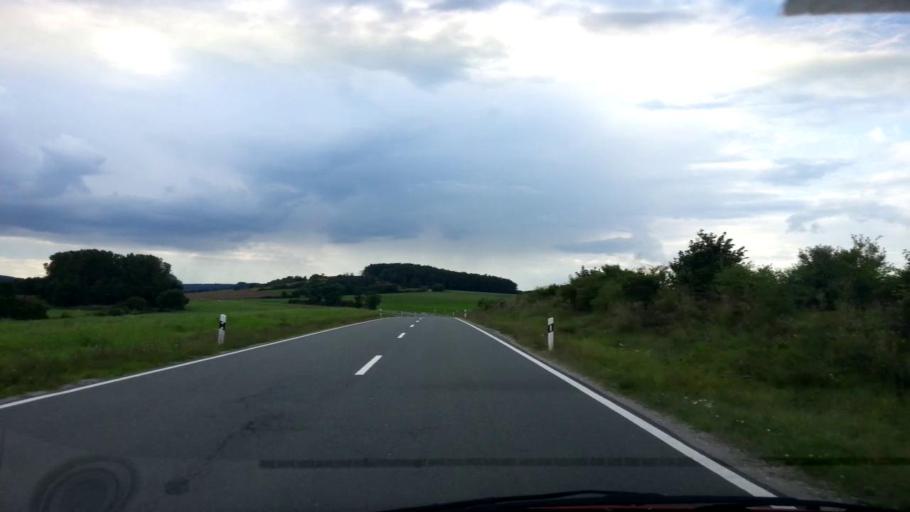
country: DE
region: Bavaria
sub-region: Regierungsbezirk Mittelfranken
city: Burghaslach
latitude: 49.7337
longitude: 10.5842
